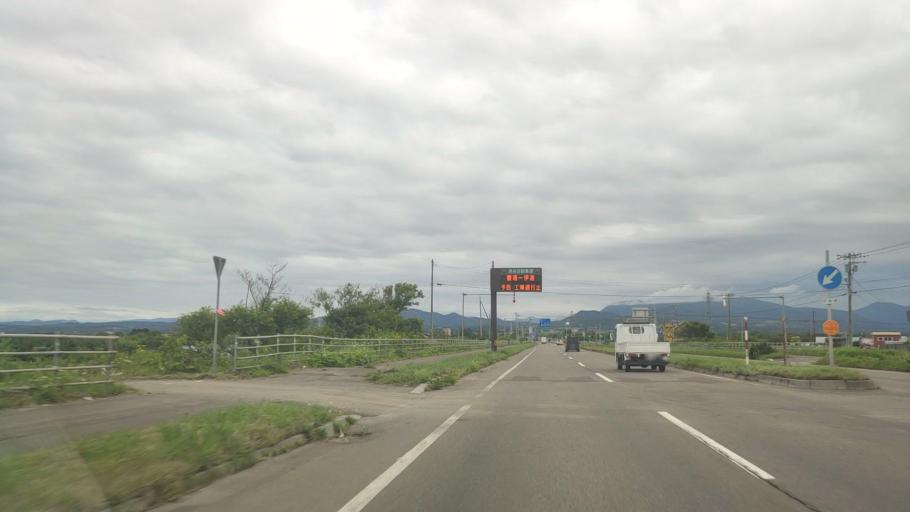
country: JP
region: Hokkaido
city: Nanae
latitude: 42.2695
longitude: 140.2726
